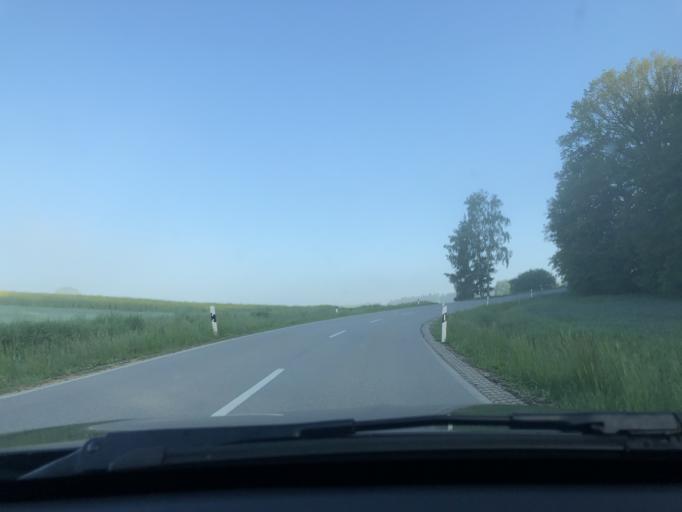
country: DE
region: Bavaria
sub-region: Upper Bavaria
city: Kirchdorf
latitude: 48.4689
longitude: 11.6398
